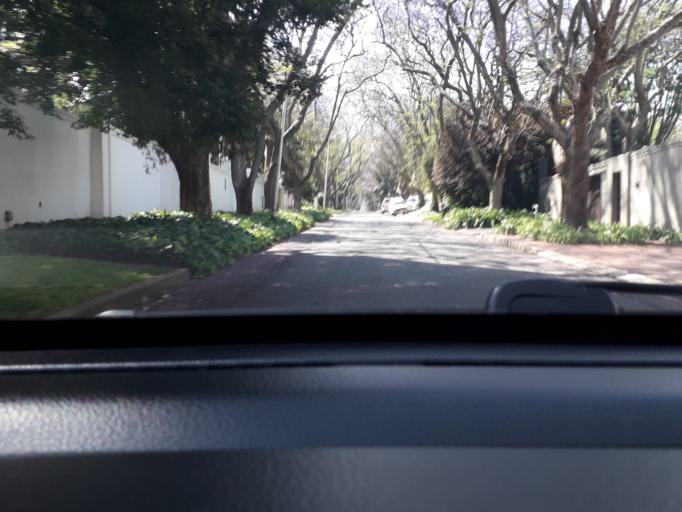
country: ZA
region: Gauteng
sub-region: City of Johannesburg Metropolitan Municipality
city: Johannesburg
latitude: -26.1402
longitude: 28.0502
